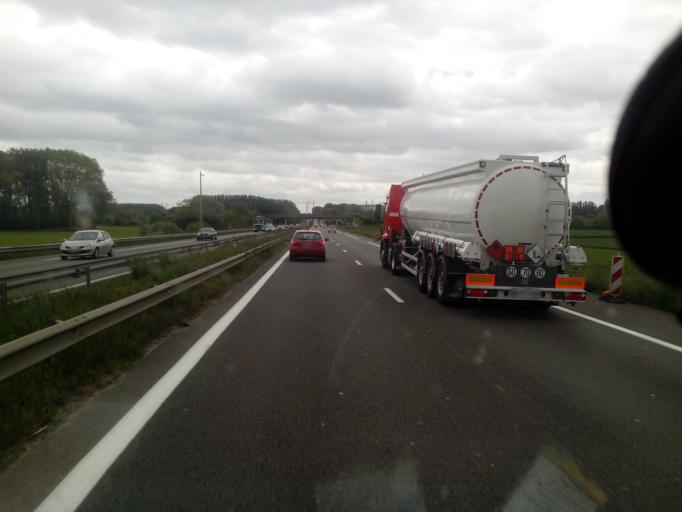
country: FR
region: Nord-Pas-de-Calais
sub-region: Departement du Nord
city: Ennetieres-en-Weppes
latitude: 50.6483
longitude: 2.9244
